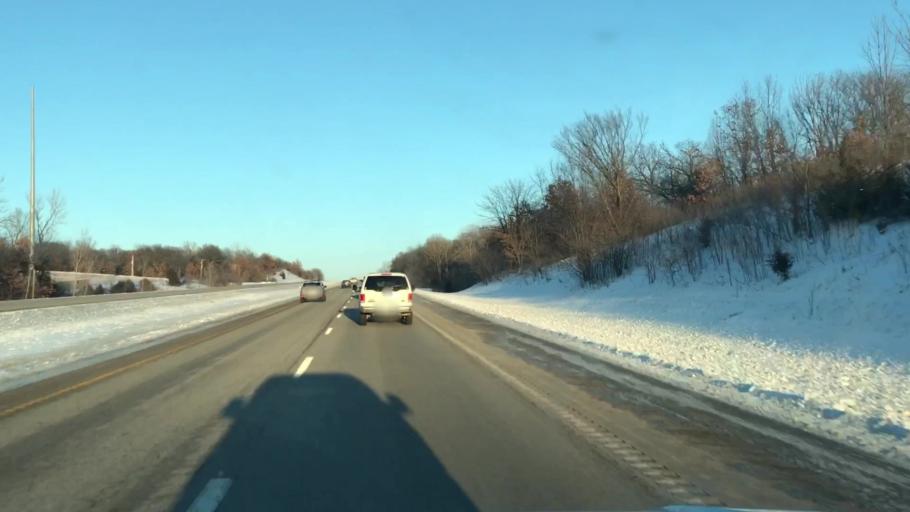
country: US
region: Missouri
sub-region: Clinton County
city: Gower
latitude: 39.7513
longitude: -94.5945
